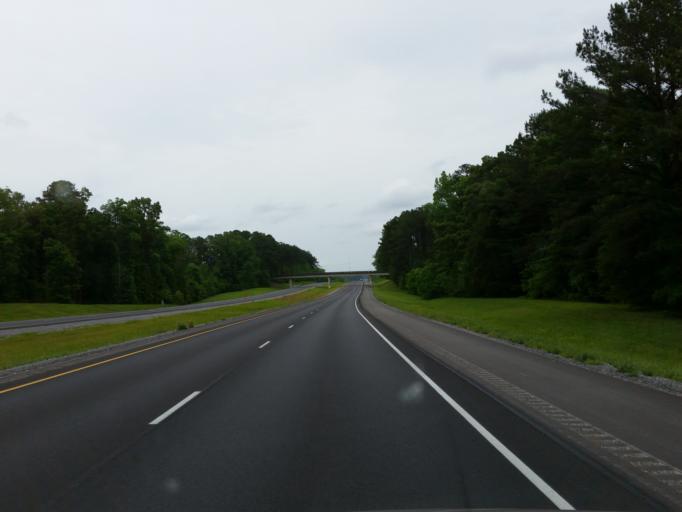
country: US
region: Mississippi
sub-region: Jones County
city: Sharon
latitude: 31.9279
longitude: -89.0001
